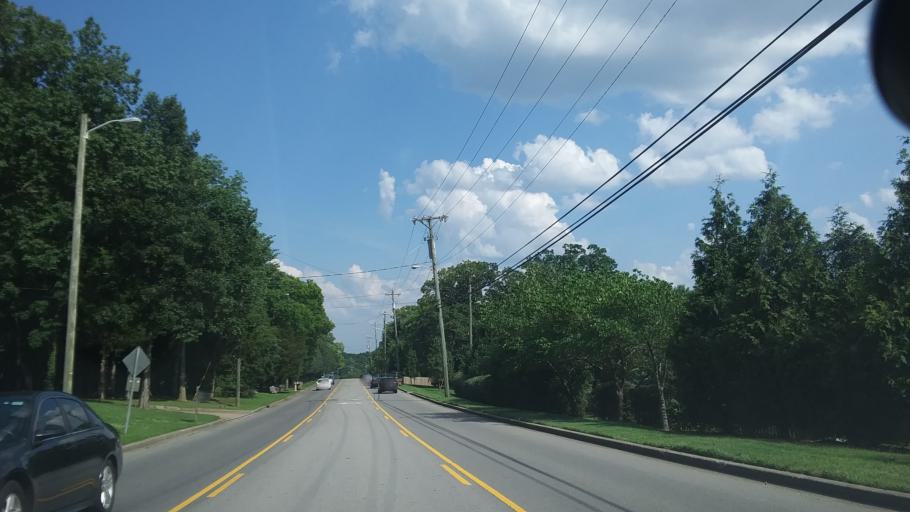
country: US
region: Tennessee
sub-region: Rutherford County
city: La Vergne
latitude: 36.0937
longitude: -86.6336
